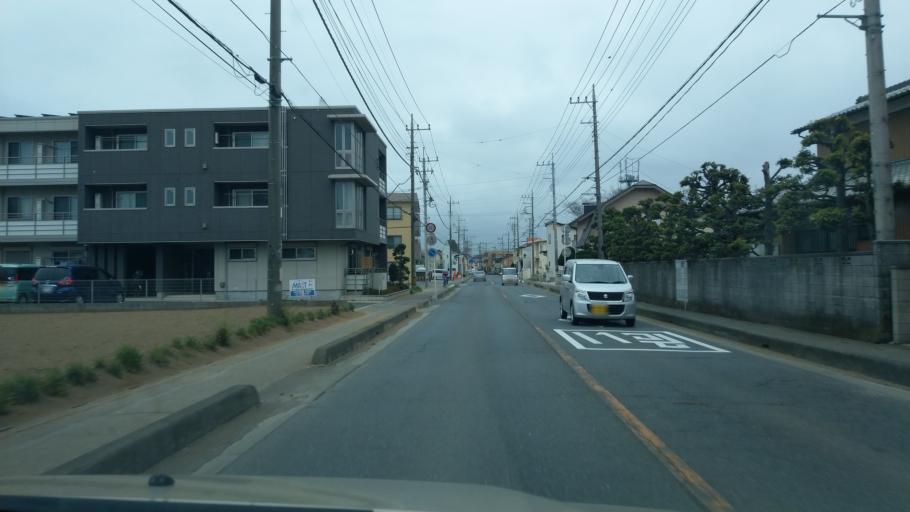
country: JP
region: Saitama
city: Saitama
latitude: 35.9265
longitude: 139.6560
